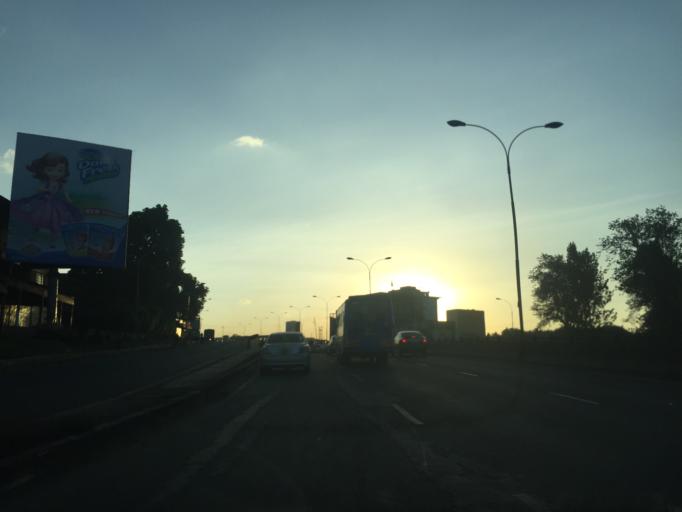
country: KE
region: Nairobi Area
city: Pumwani
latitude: -1.2645
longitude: 36.8369
